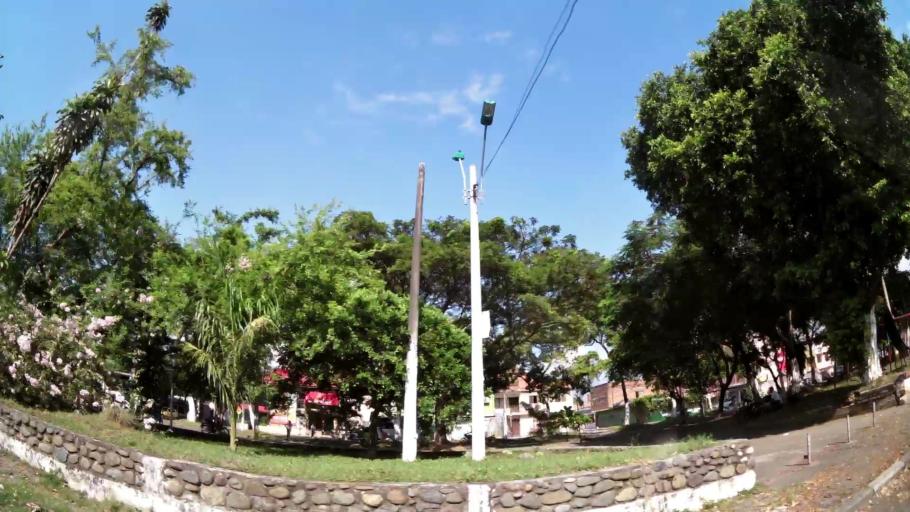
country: CO
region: Valle del Cauca
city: Cali
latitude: 3.4213
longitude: -76.5170
